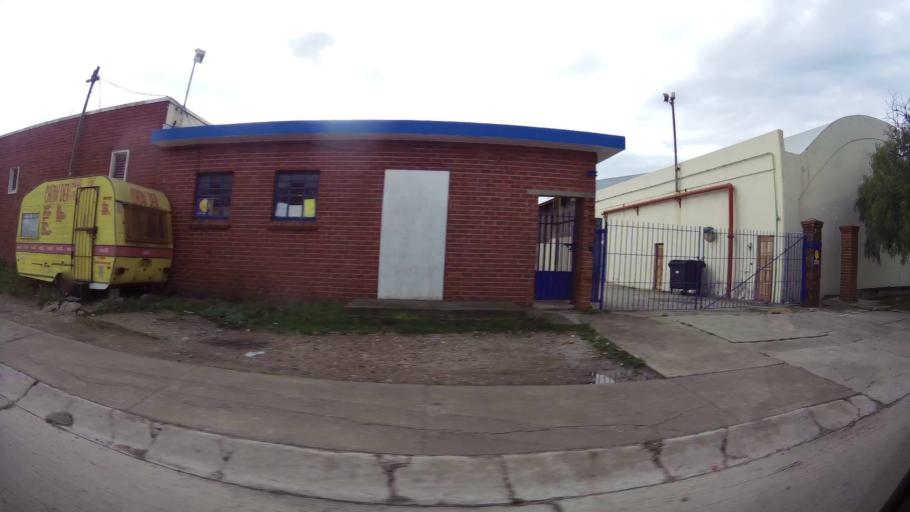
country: ZA
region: Eastern Cape
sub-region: Nelson Mandela Bay Metropolitan Municipality
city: Port Elizabeth
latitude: -33.9268
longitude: 25.5790
